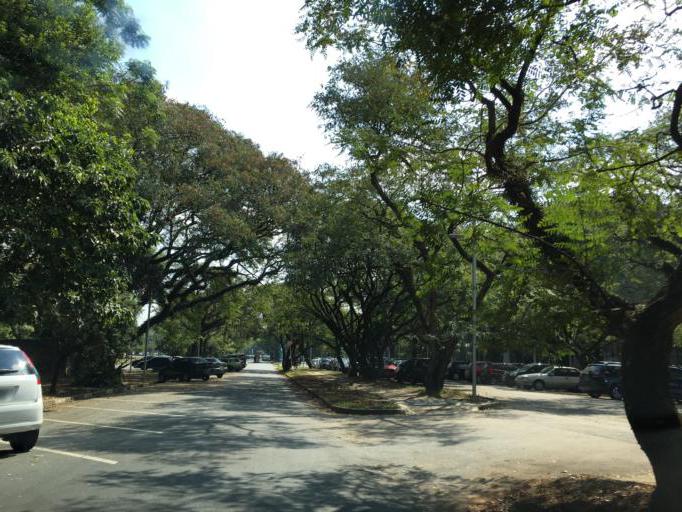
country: BR
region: Sao Paulo
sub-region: Osasco
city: Osasco
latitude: -23.5612
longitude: -46.7294
